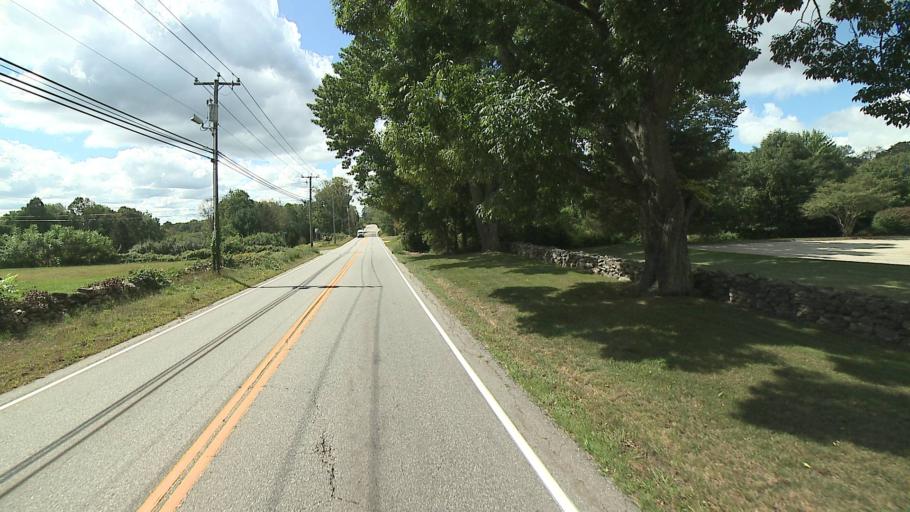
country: US
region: Connecticut
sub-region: Tolland County
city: Storrs
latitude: 41.8755
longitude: -72.1178
